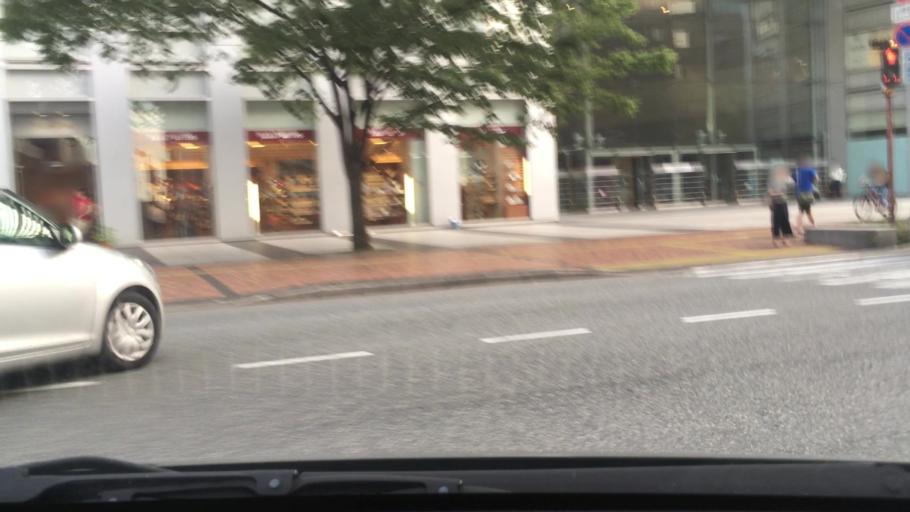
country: JP
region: Fukuoka
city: Fukuoka-shi
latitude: 33.5922
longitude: 130.4024
